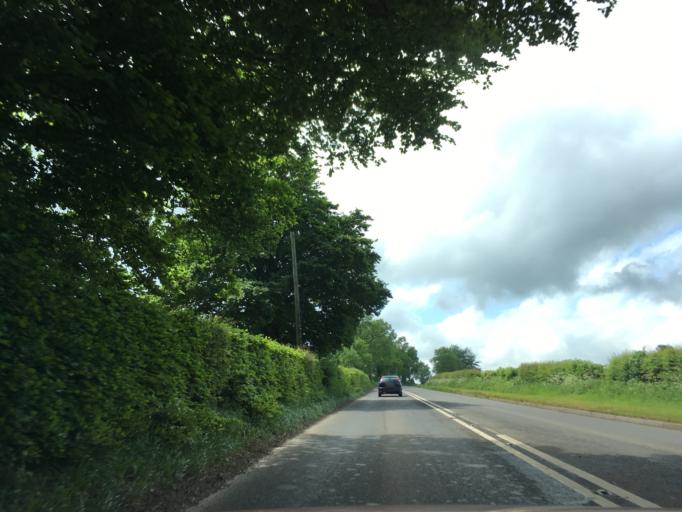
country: GB
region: England
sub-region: Devon
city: Uffculme
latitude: 50.9347
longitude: -3.3083
